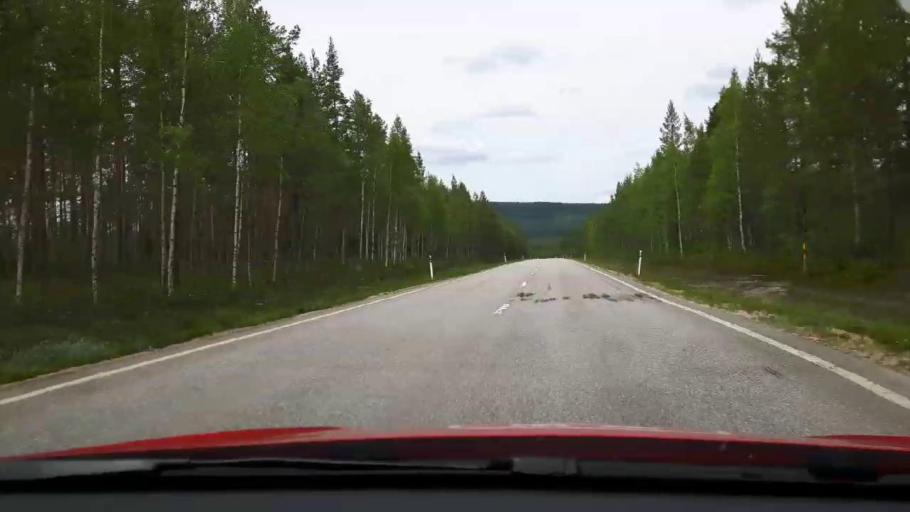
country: SE
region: Jaemtland
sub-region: Harjedalens Kommun
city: Sveg
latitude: 62.0846
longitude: 14.2528
